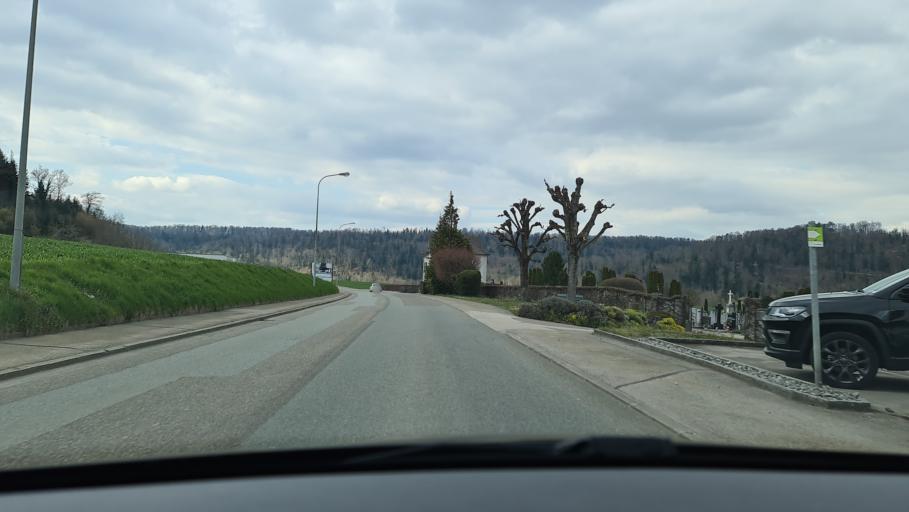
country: CH
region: Jura
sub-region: Porrentruy District
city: Porrentruy
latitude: 47.4259
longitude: 7.0775
